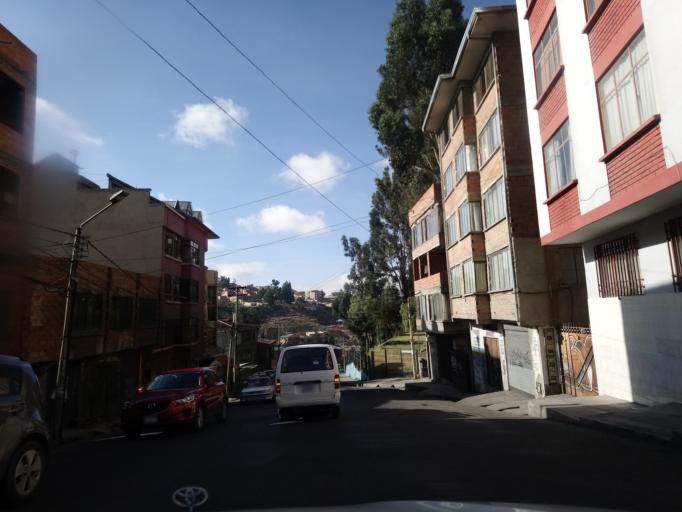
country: BO
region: La Paz
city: La Paz
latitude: -16.5024
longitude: -68.1159
